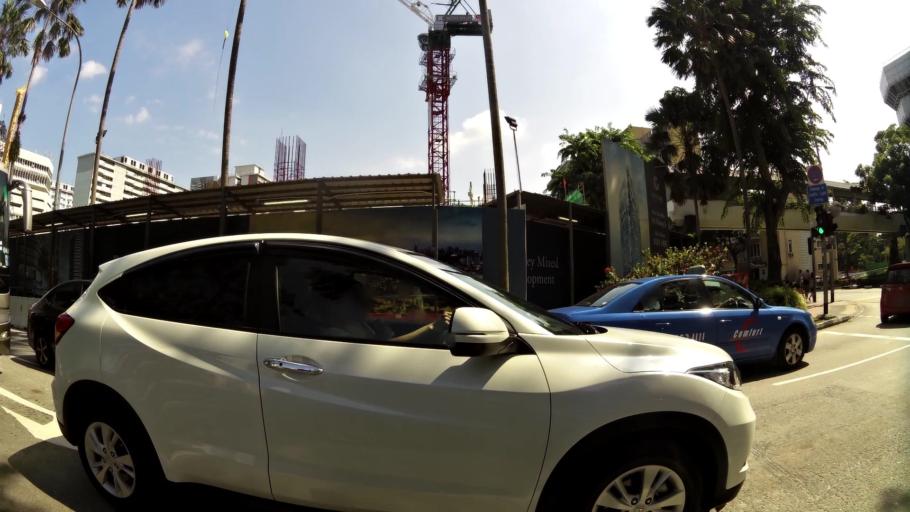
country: SG
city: Singapore
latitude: 1.3018
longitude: 103.8622
